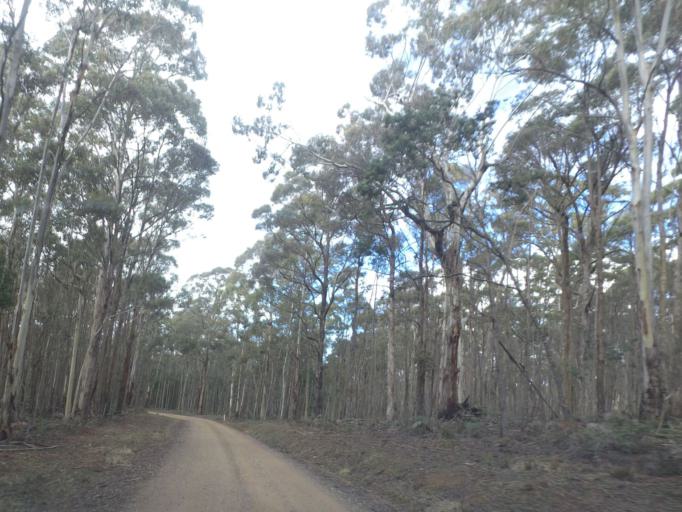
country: AU
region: Victoria
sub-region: Moorabool
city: Bacchus Marsh
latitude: -37.4295
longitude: 144.4332
